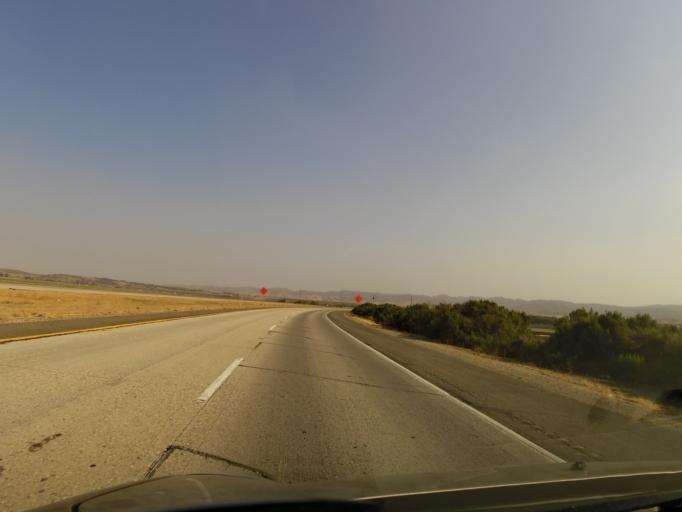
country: US
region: California
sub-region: Monterey County
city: King City
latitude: 36.1168
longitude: -121.0202
